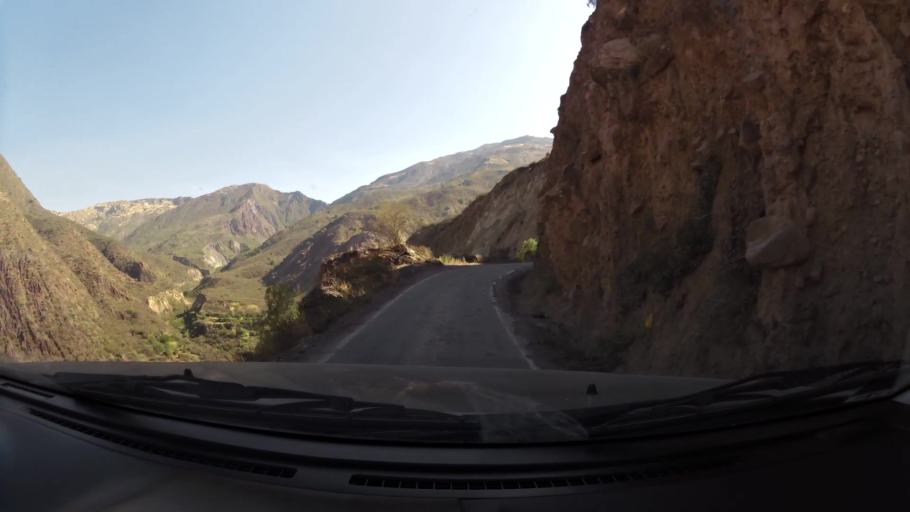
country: PE
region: Huancavelica
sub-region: Provincia de Acobamba
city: Pomacocha
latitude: -12.7858
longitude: -74.4941
